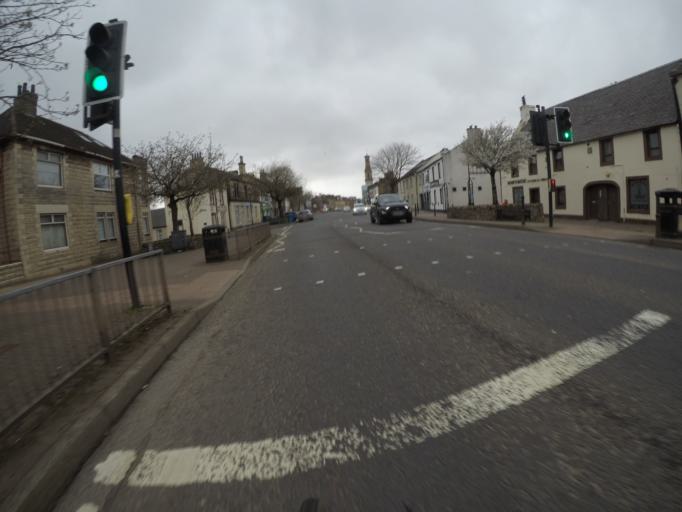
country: GB
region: Scotland
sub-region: North Ayrshire
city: Irvine
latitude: 55.6137
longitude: -4.6629
